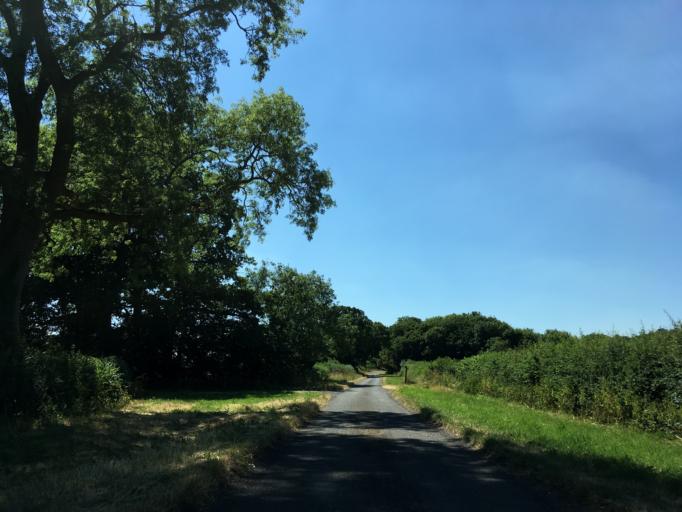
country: GB
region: England
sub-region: Wiltshire
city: Norton
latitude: 51.5716
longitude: -2.1881
